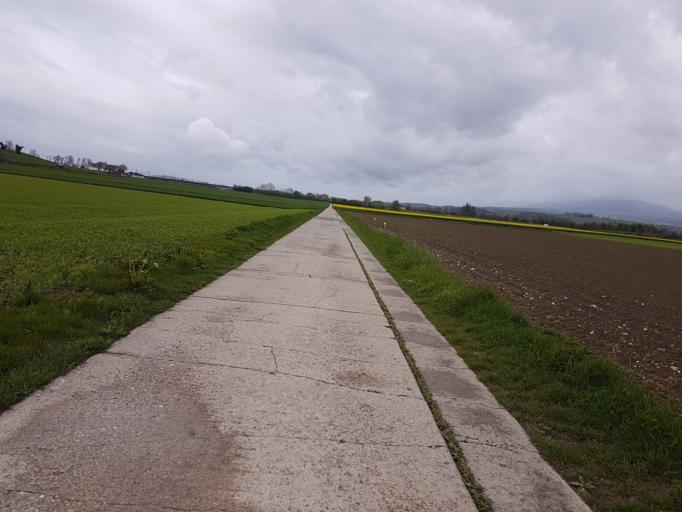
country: CH
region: Vaud
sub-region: Jura-Nord vaudois District
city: Chavornay
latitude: 46.7286
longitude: 6.5788
